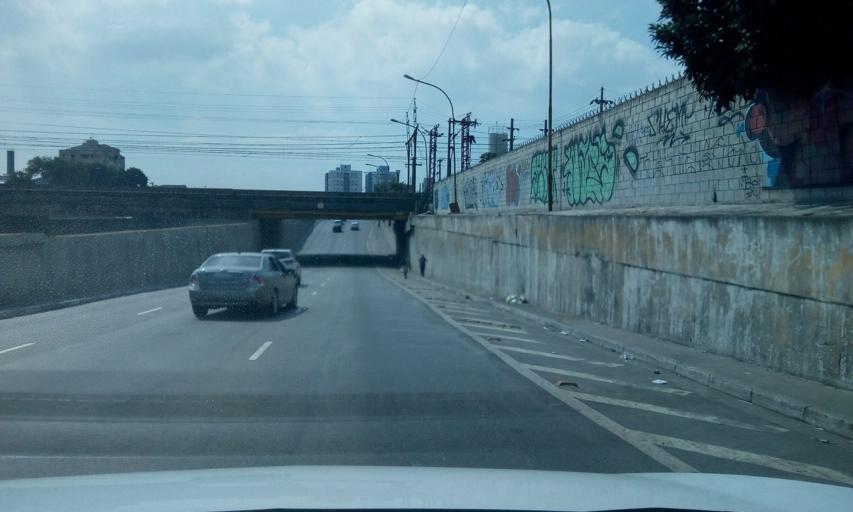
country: BR
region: Sao Paulo
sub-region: Sao Paulo
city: Sao Paulo
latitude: -23.5383
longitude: -46.6266
